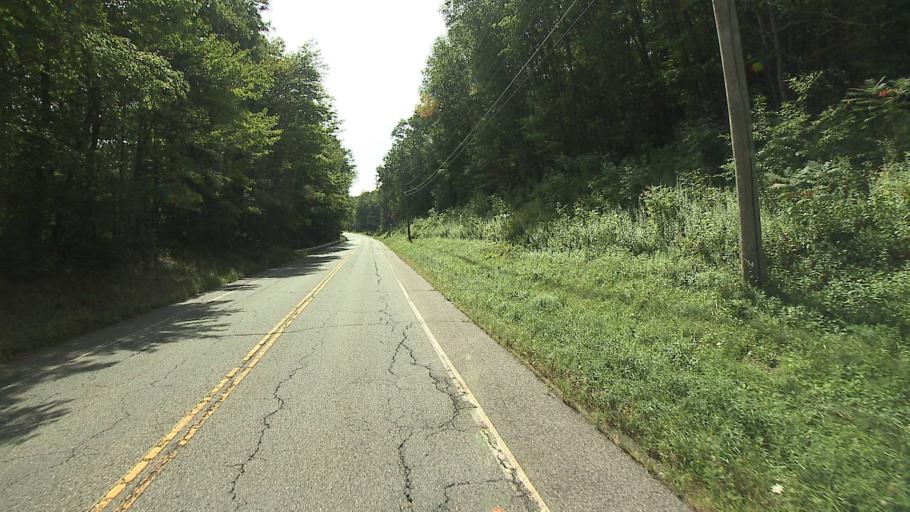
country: US
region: Connecticut
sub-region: Litchfield County
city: Thomaston
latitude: 41.6999
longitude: -73.1115
